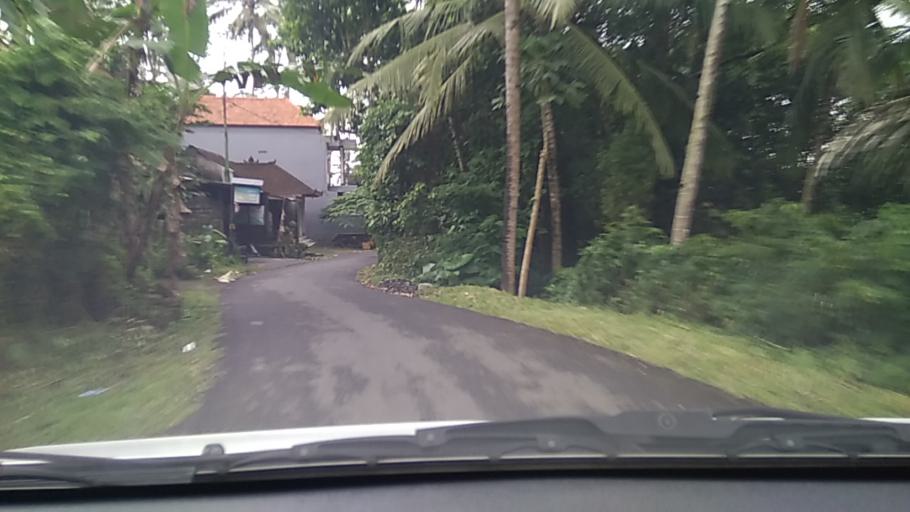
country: ID
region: Bali
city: Tegalalang
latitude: -8.4243
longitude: 115.2797
